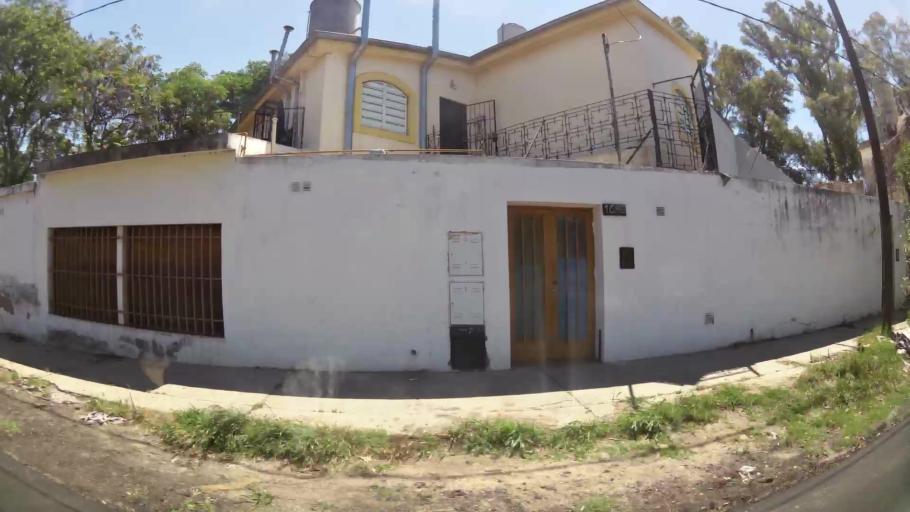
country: AR
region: Cordoba
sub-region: Departamento de Capital
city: Cordoba
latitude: -31.3933
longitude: -64.1932
